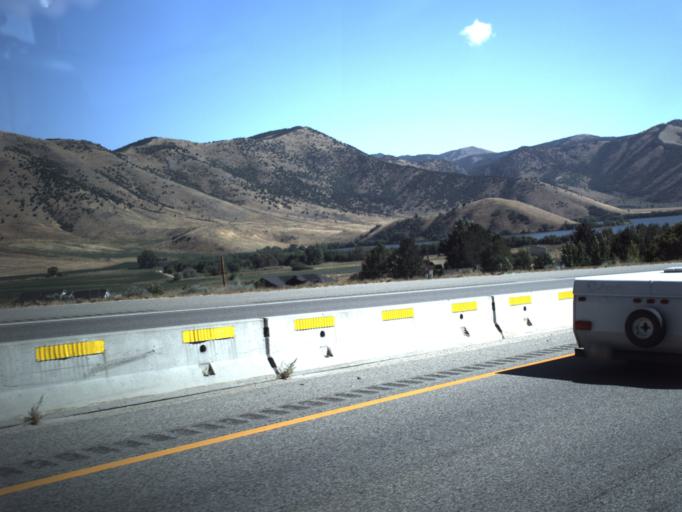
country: US
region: Utah
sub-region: Box Elder County
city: Brigham City
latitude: 41.5188
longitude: -111.9409
